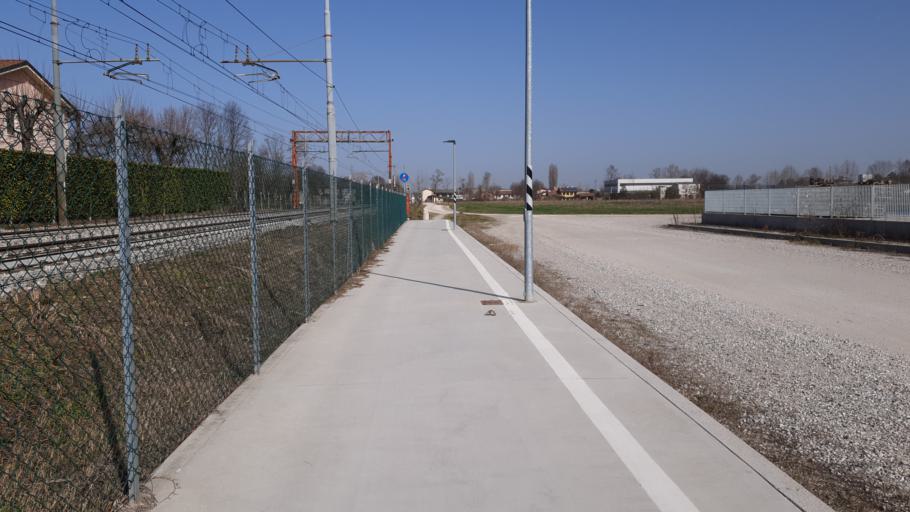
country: IT
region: Veneto
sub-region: Provincia di Padova
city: Camposampiero
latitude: 45.5472
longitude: 11.9195
